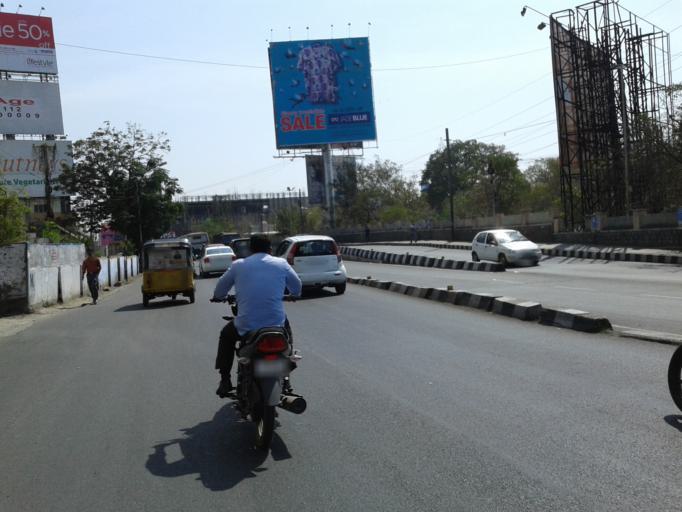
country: IN
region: Telangana
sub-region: Hyderabad
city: Hyderabad
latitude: 17.4267
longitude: 78.4466
